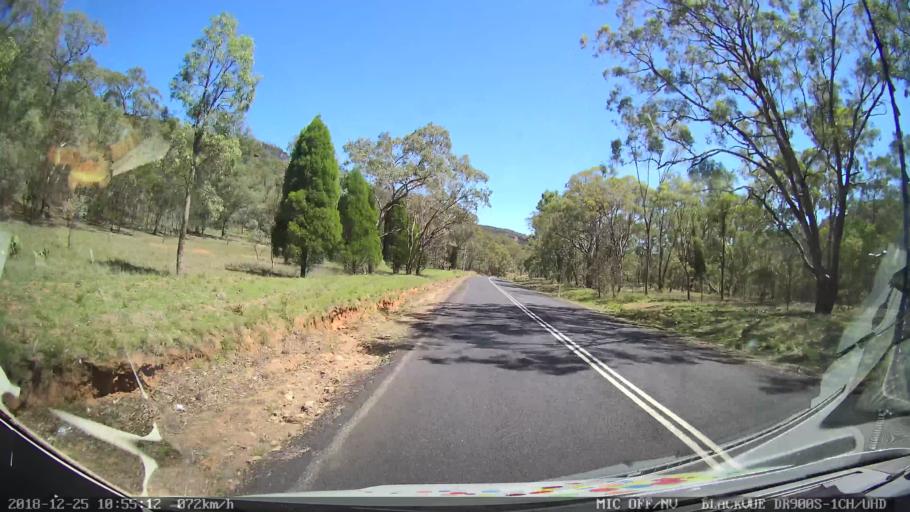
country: AU
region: New South Wales
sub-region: Upper Hunter Shire
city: Merriwa
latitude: -32.4014
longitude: 150.2725
